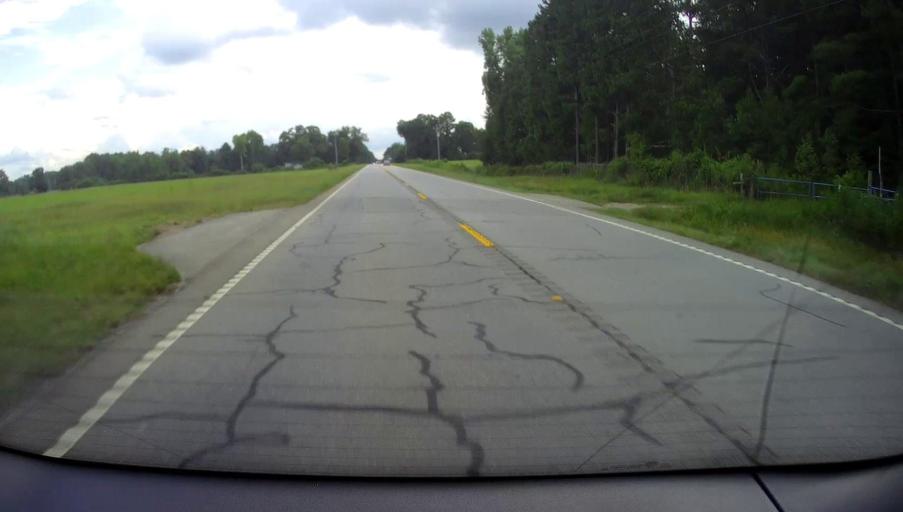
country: US
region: Georgia
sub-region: Coweta County
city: Senoia
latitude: 33.2045
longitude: -84.5804
